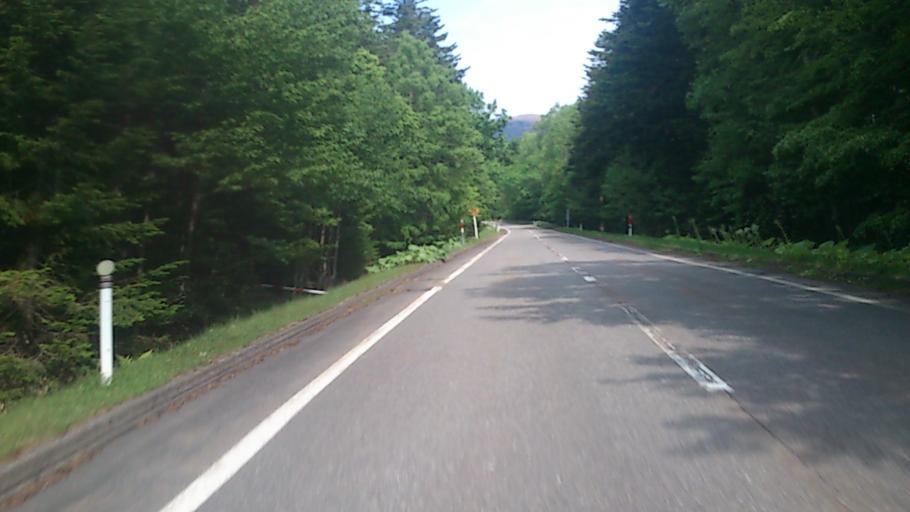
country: JP
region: Hokkaido
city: Kitami
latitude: 43.4020
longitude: 143.9751
